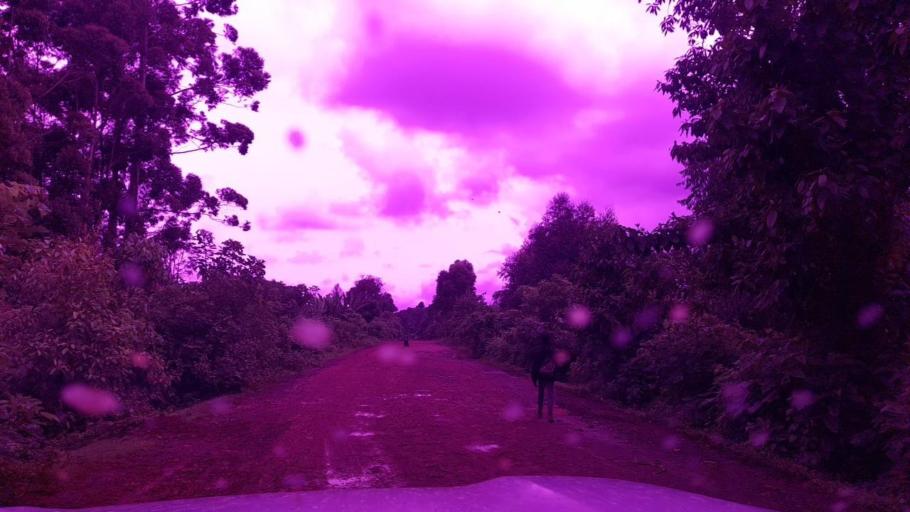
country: ET
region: Southern Nations, Nationalities, and People's Region
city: Tippi
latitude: 7.5831
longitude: 35.6710
